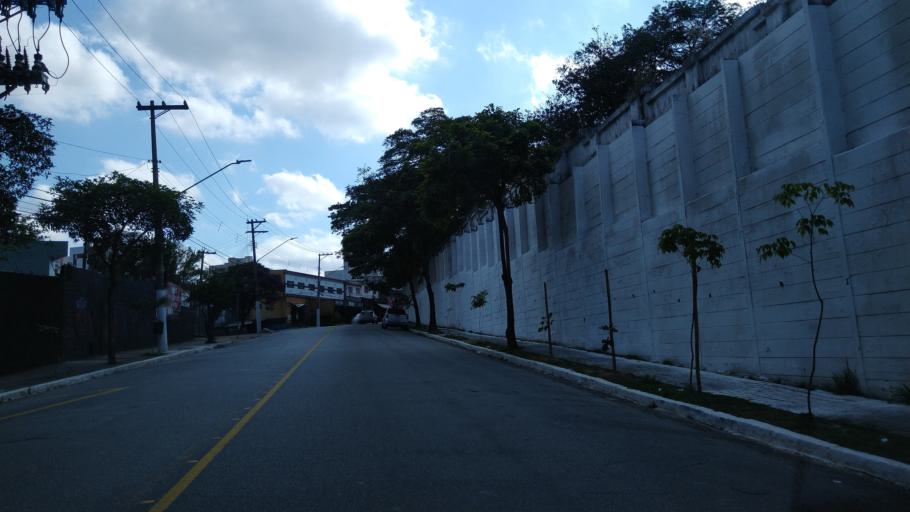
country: BR
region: Sao Paulo
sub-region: Sao Paulo
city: Sao Paulo
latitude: -23.4972
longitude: -46.6380
